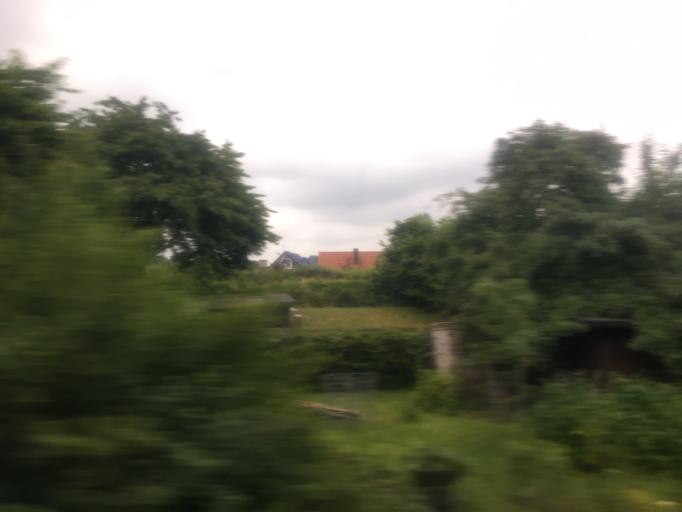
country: DE
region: North Rhine-Westphalia
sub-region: Regierungsbezirk Munster
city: Steinfurt
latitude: 52.1421
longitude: 7.3361
